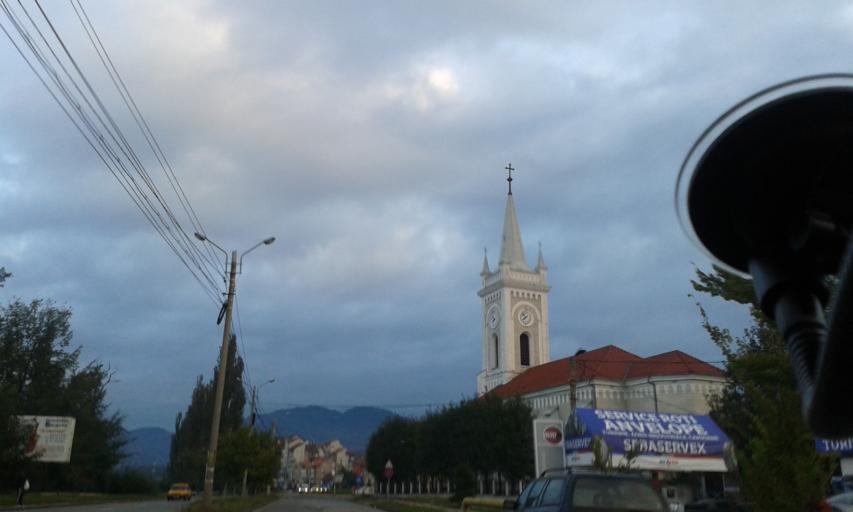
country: RO
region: Hunedoara
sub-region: Municipiul Petrosani
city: Petrosani
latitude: 45.4178
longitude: 23.3676
